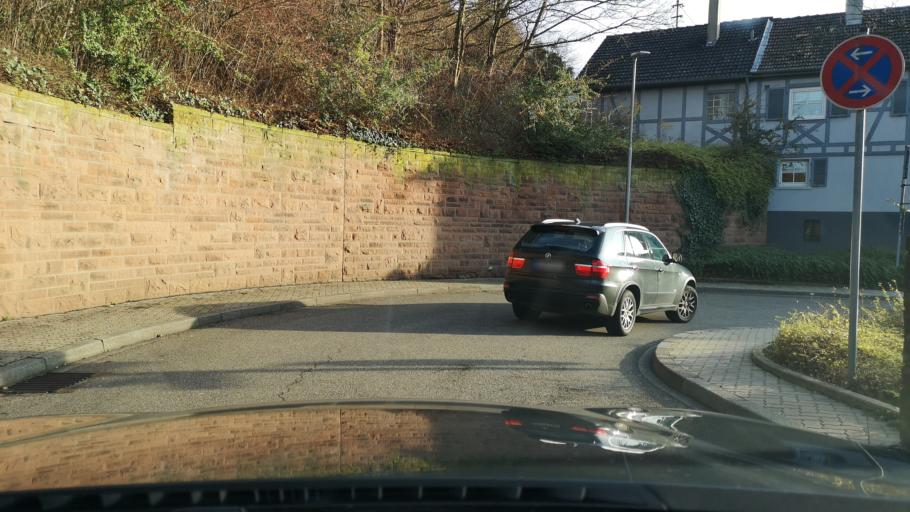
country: DE
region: Baden-Wuerttemberg
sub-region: Karlsruhe Region
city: Ettlingen
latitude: 48.9592
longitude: 8.4665
